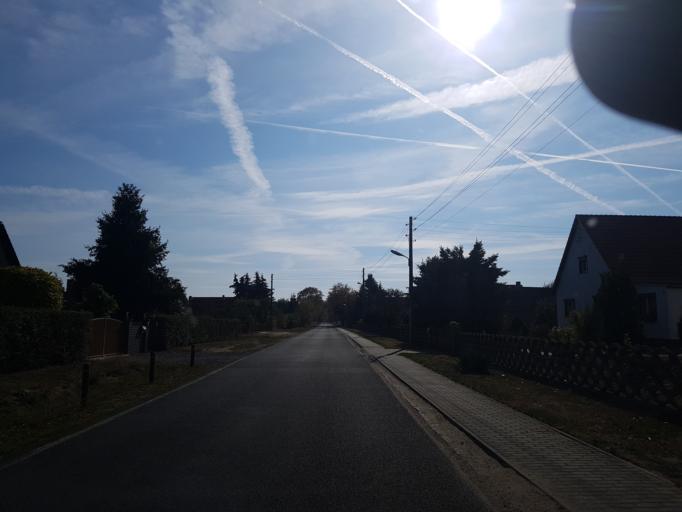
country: DE
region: Brandenburg
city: Lebusa
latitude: 51.8293
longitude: 13.3904
